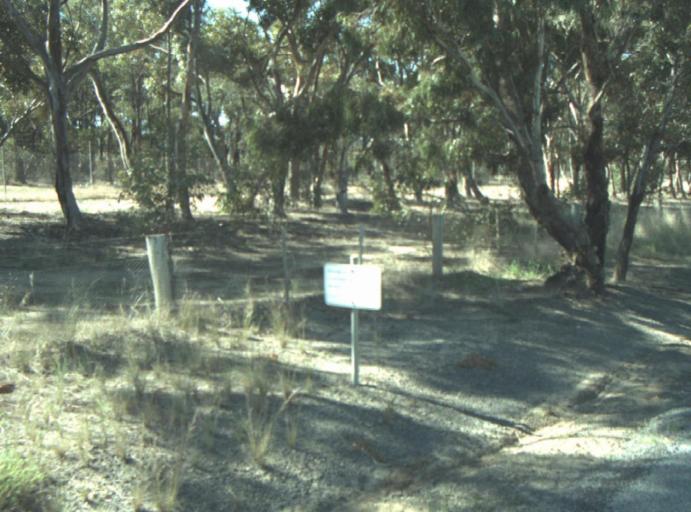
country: AU
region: Victoria
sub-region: Greater Geelong
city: Lara
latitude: -37.9163
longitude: 144.3973
